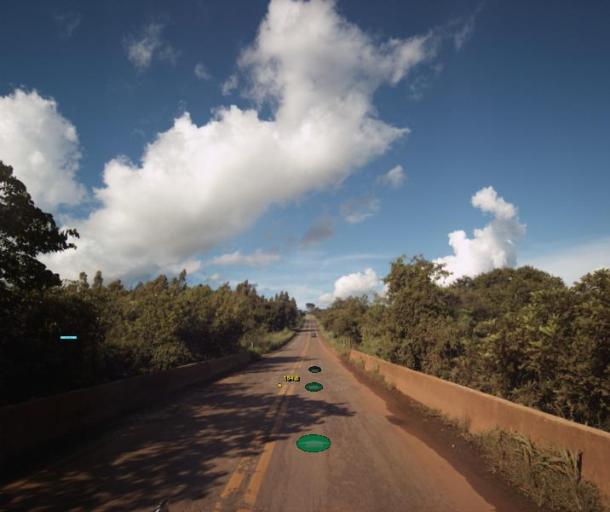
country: BR
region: Goias
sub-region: Itaberai
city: Itaberai
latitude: -15.9998
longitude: -49.7472
